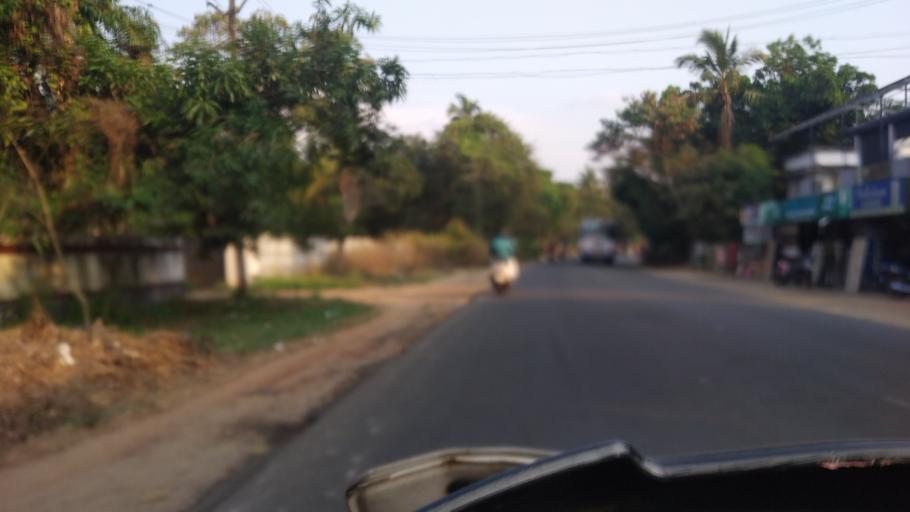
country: IN
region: Kerala
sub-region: Thrissur District
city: Thanniyam
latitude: 10.3615
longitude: 76.1261
